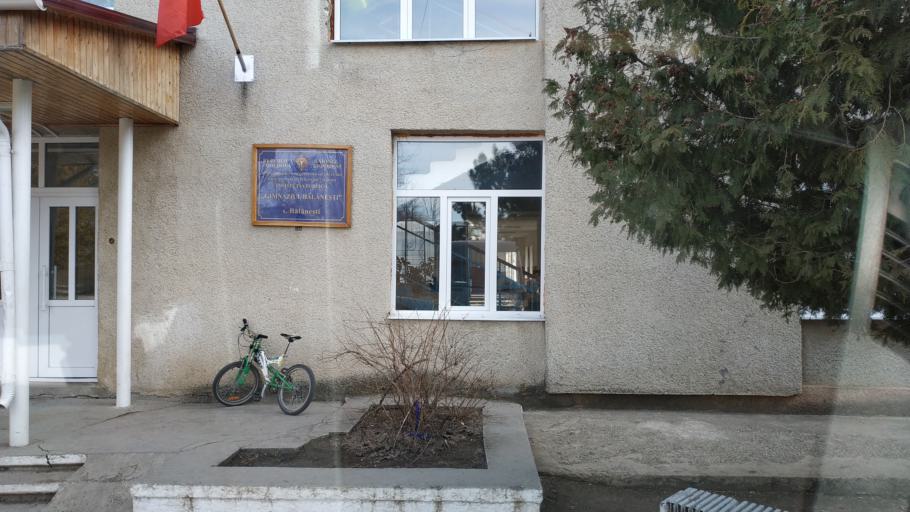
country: MD
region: Nisporeni
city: Nisporeni
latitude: 47.1943
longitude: 28.0667
